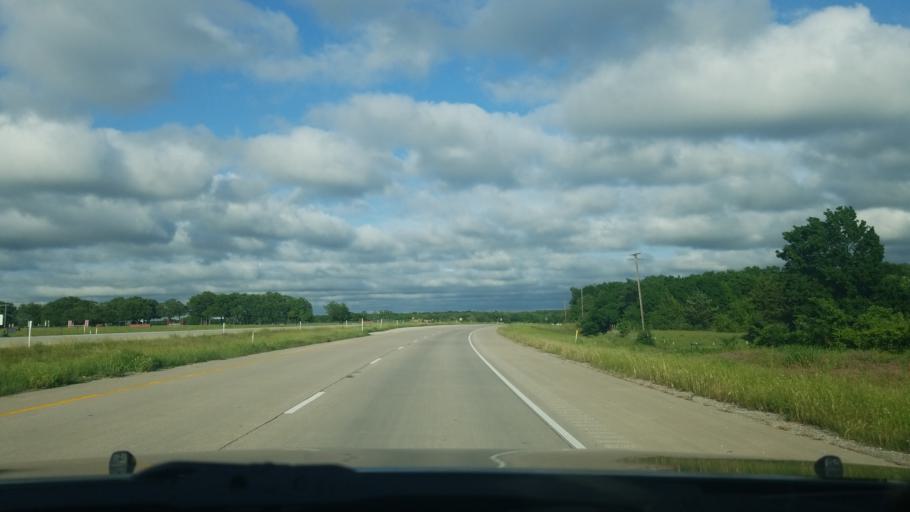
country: US
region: Texas
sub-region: Denton County
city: Ponder
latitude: 33.2509
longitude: -97.4137
